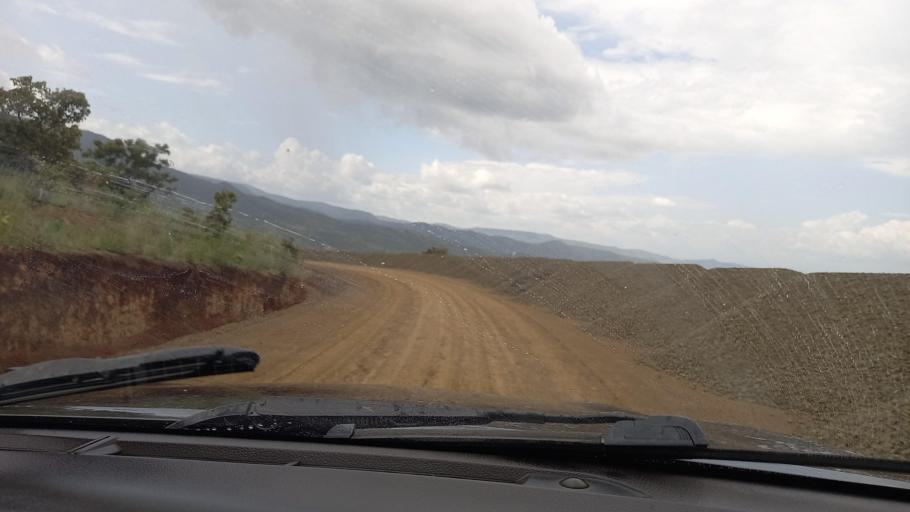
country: ET
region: Southern Nations, Nationalities, and People's Region
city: Mizan Teferi
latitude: 6.1856
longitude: 35.6914
